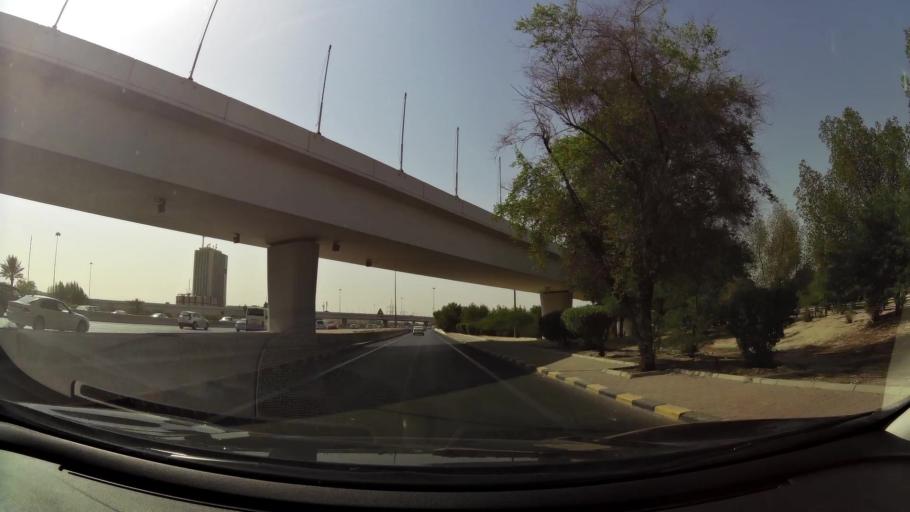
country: KW
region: Muhafazat Hawalli
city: Hawalli
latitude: 29.3077
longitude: 48.0234
